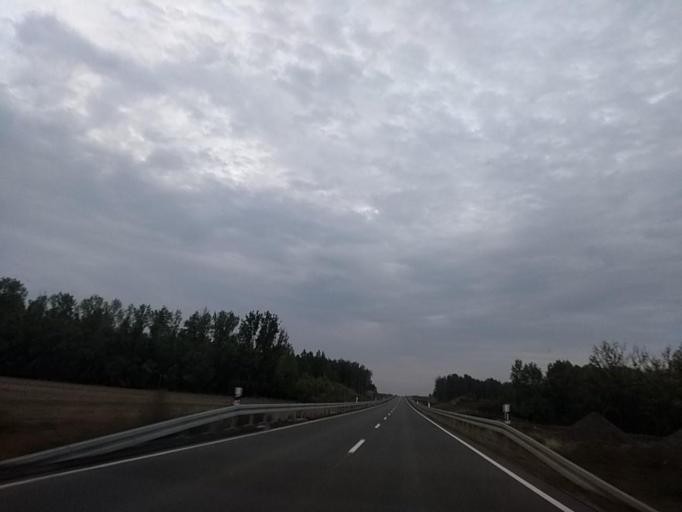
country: DE
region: Saxony-Anhalt
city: Muschwitz
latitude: 51.1734
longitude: 12.1230
